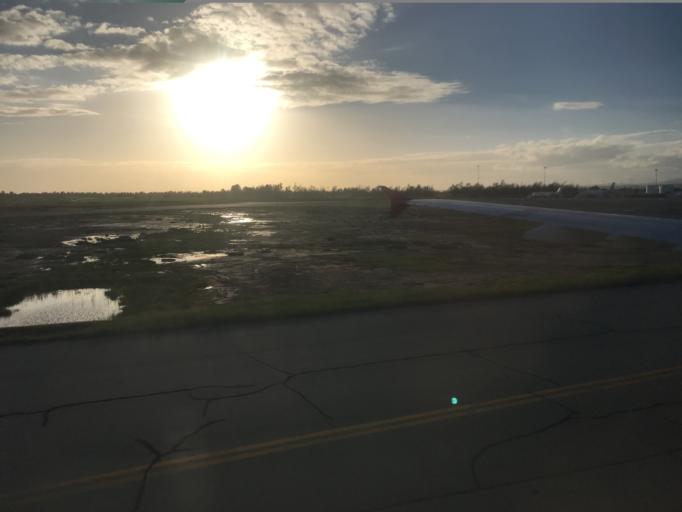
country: CY
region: Larnaka
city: Meneou
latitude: 34.8666
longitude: 33.6135
